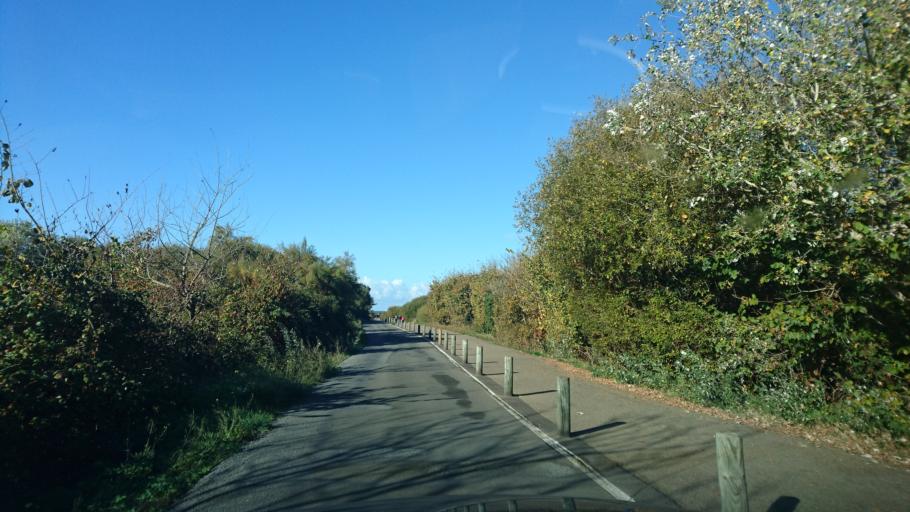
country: FR
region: Pays de la Loire
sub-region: Departement de la Vendee
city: Les Sables-d'Olonne
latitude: 46.5028
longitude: -1.8107
